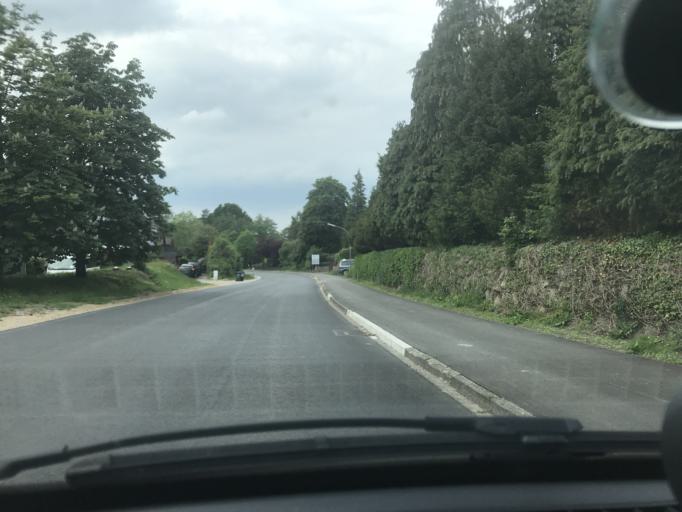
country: DE
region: Schleswig-Holstein
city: Rausdorf
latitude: 53.5877
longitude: 10.3318
